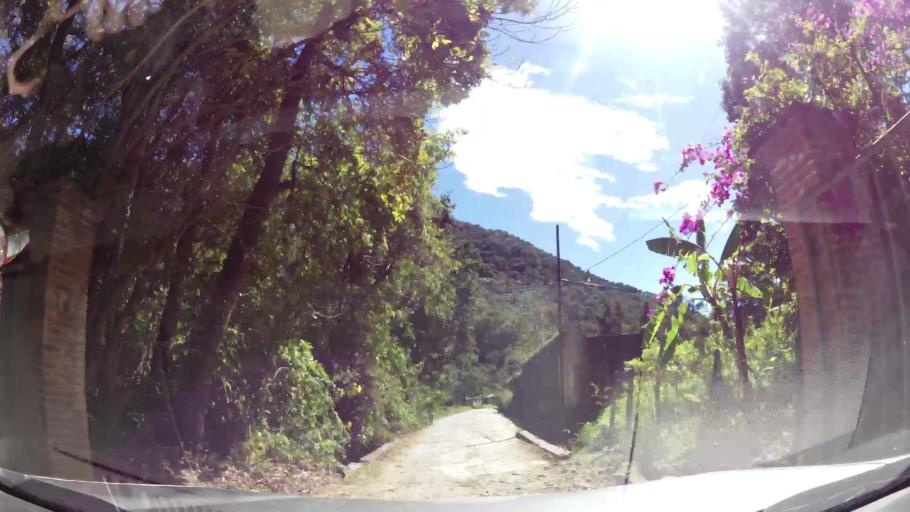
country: GT
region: Solola
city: Panajachel
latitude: 14.7499
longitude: -91.1650
